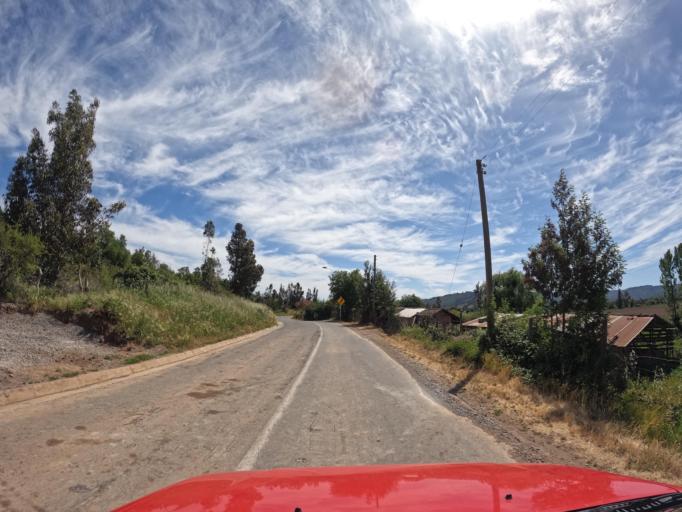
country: CL
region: Maule
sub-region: Provincia de Talca
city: Talca
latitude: -34.9895
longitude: -71.8402
